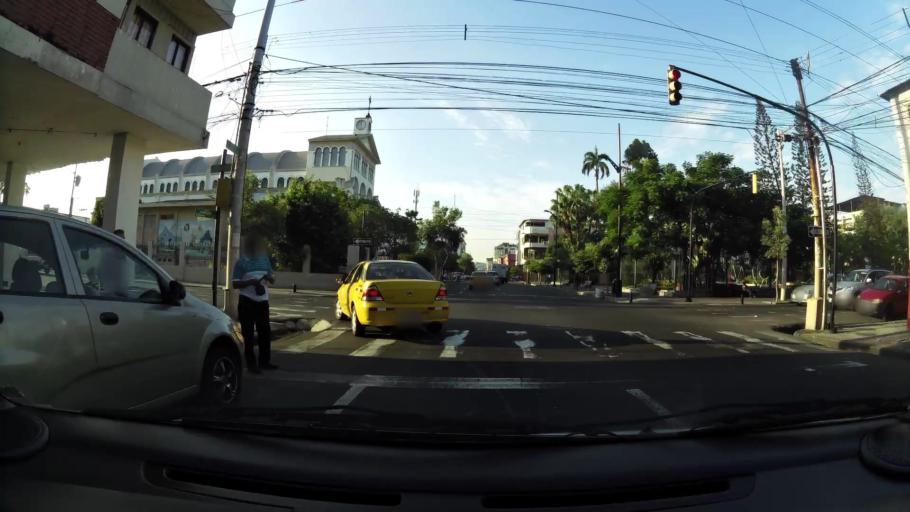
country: EC
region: Guayas
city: Guayaquil
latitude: -2.2099
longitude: -79.8875
